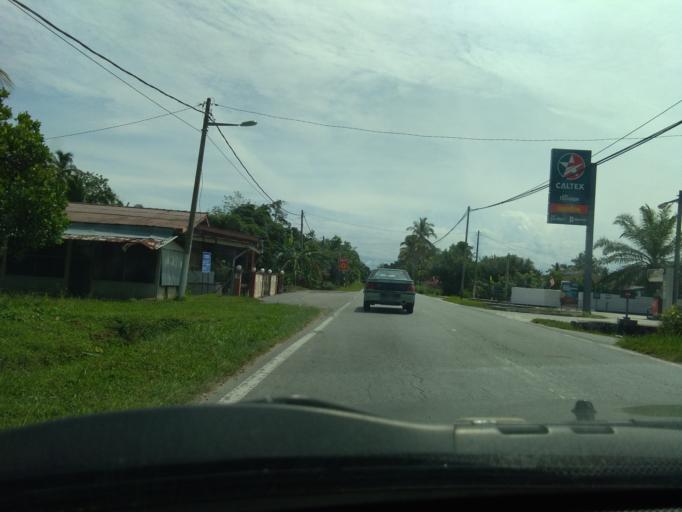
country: MY
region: Perak
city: Bagan Serai
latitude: 5.0438
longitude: 100.5777
